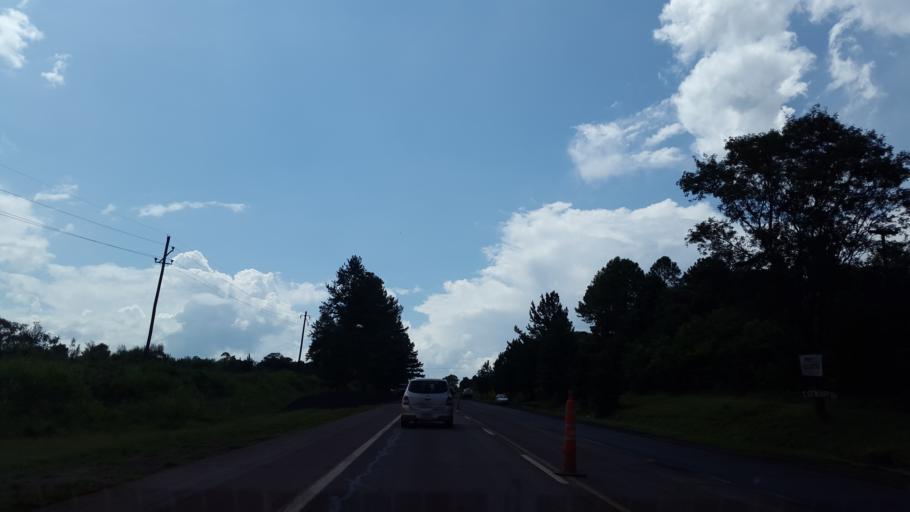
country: AR
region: Misiones
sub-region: Departamento de Eldorado
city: Eldorado
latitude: -26.4613
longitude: -54.6436
